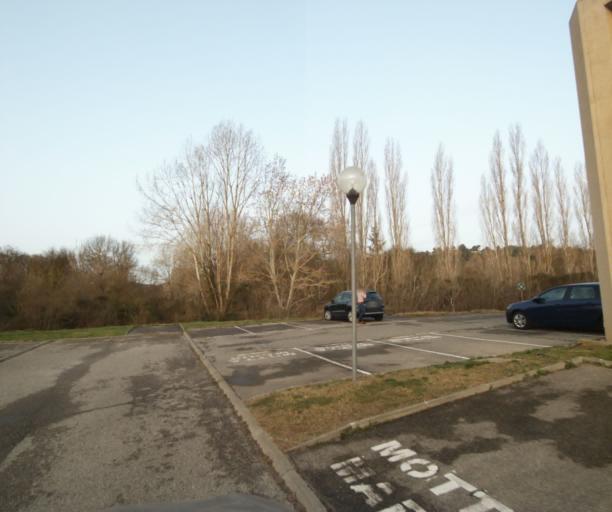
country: FR
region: Provence-Alpes-Cote d'Azur
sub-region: Departement des Bouches-du-Rhone
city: Meyreuil
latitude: 43.4925
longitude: 5.5224
